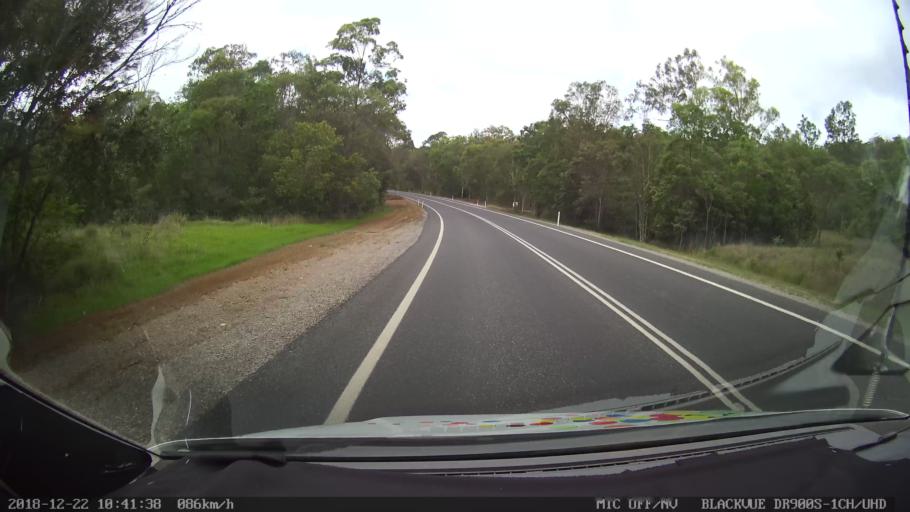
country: AU
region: New South Wales
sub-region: Clarence Valley
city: South Grafton
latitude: -29.6347
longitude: 152.7632
